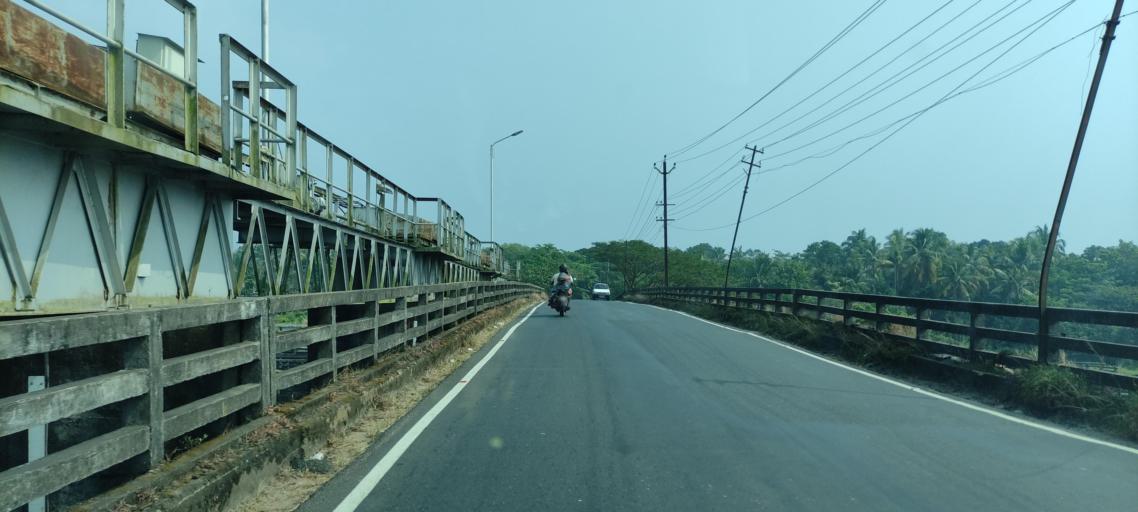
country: IN
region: Kerala
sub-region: Alappuzha
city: Shertallai
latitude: 9.6723
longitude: 76.4051
